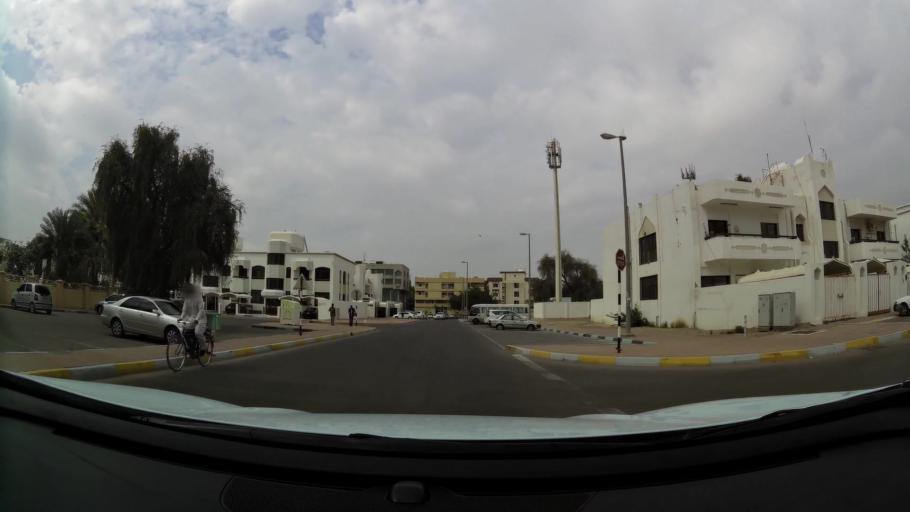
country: AE
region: Abu Dhabi
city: Al Ain
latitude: 24.2235
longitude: 55.7726
